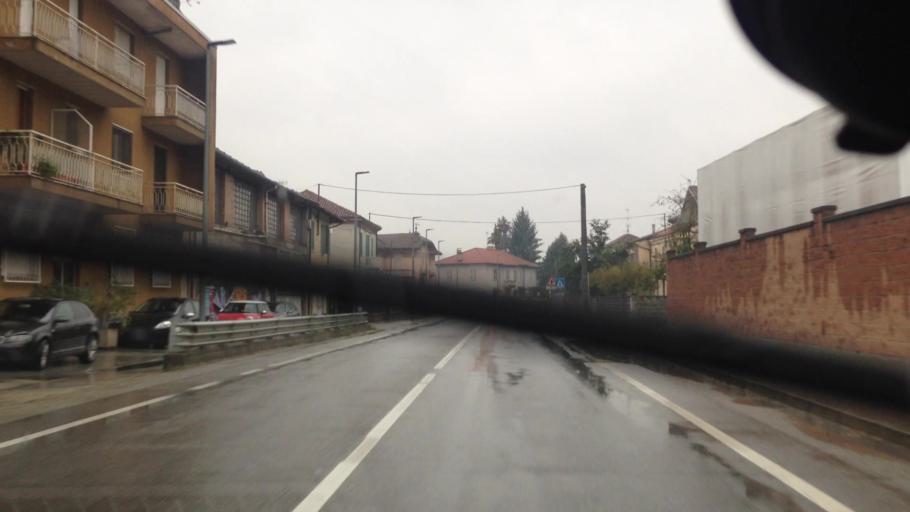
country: IT
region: Piedmont
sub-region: Provincia di Asti
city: Castello di Annone
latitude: 44.8776
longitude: 8.3201
